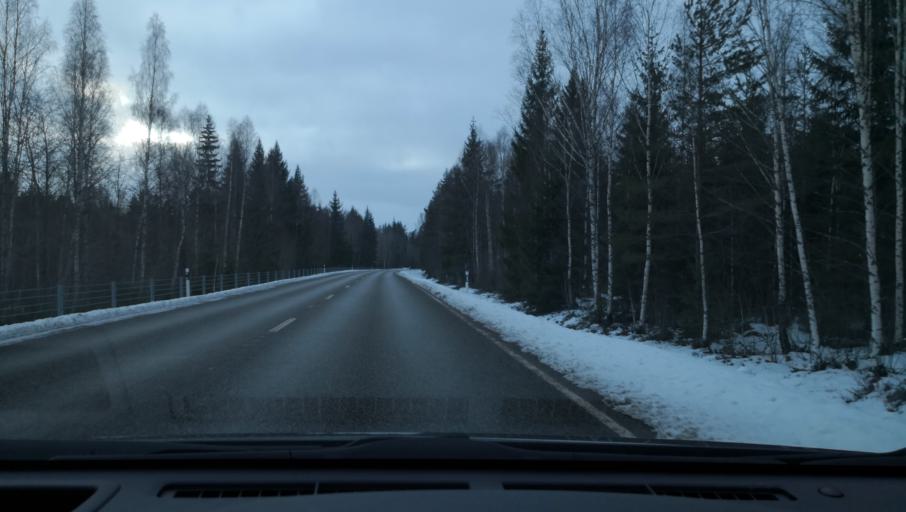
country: SE
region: Vaestmanland
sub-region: Skinnskattebergs Kommun
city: Skinnskatteberg
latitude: 59.7969
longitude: 15.8839
